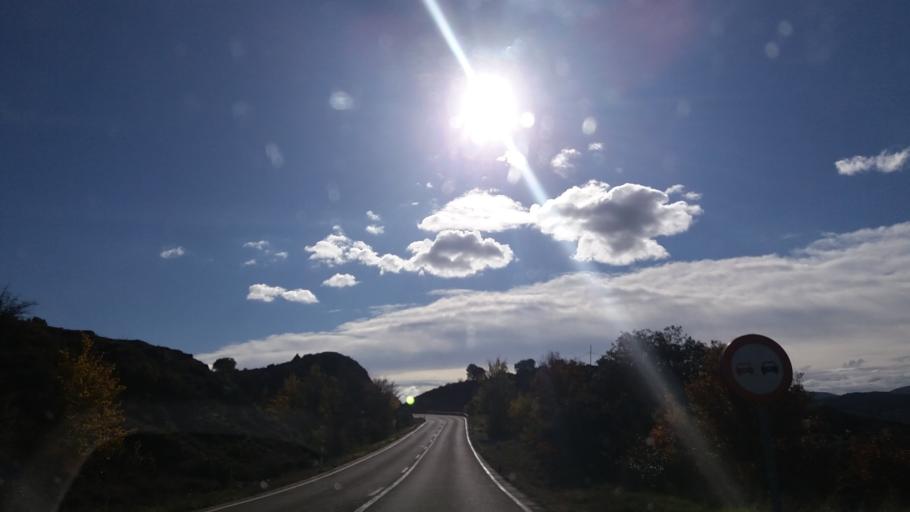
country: ES
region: Aragon
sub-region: Provincia de Zaragoza
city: Mianos
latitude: 42.6044
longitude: -0.8661
